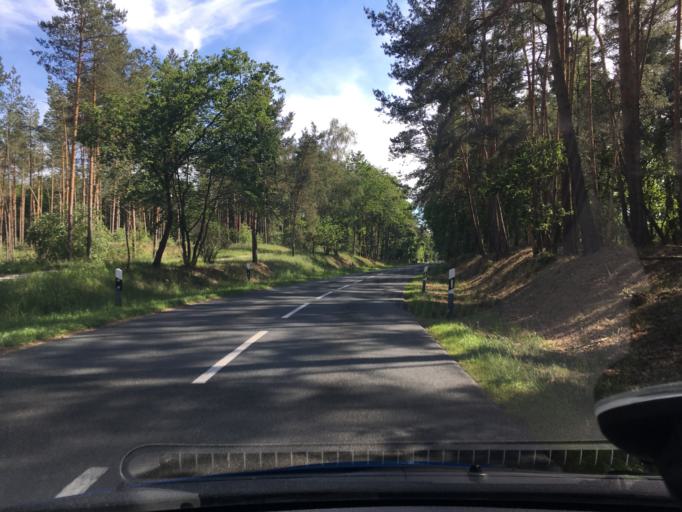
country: DE
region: Lower Saxony
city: Neu Darchau
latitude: 53.2993
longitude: 10.9314
